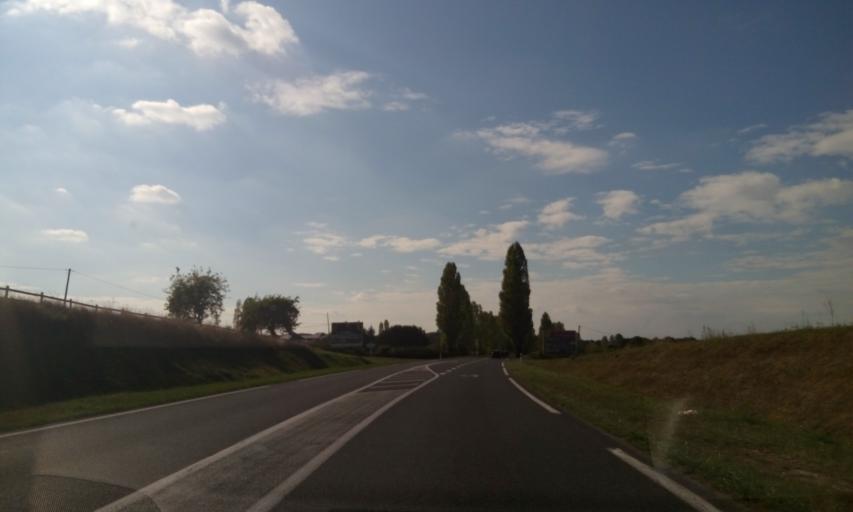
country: FR
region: Centre
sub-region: Departement d'Indre-et-Loire
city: Amboise
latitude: 47.3935
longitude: 1.0130
